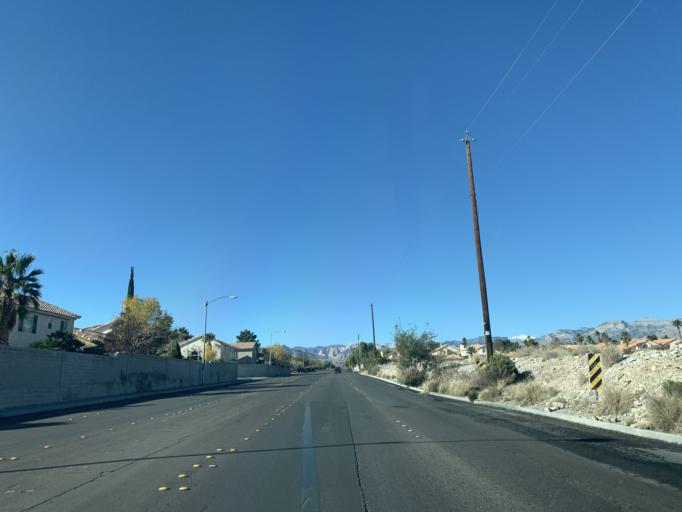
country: US
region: Nevada
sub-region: Clark County
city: Spring Valley
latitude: 36.1260
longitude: -115.2814
